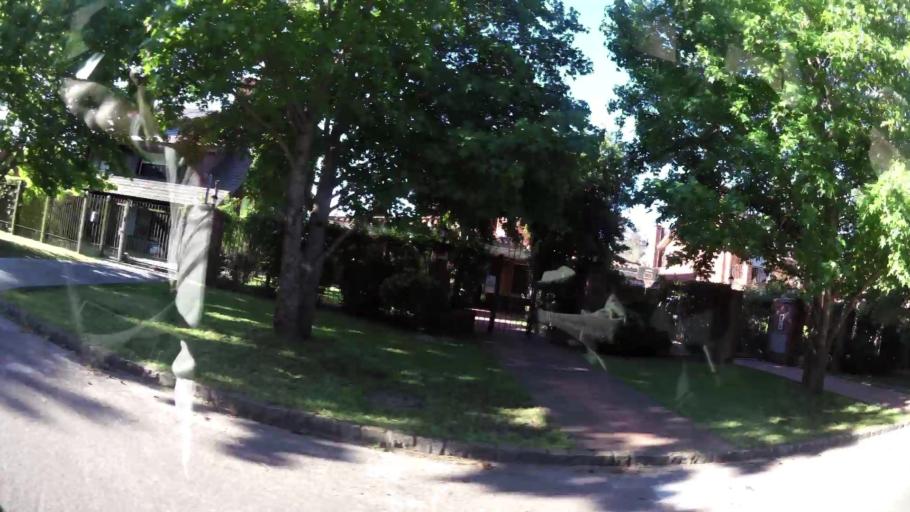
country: UY
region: Canelones
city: Paso de Carrasco
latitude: -34.8700
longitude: -56.0461
